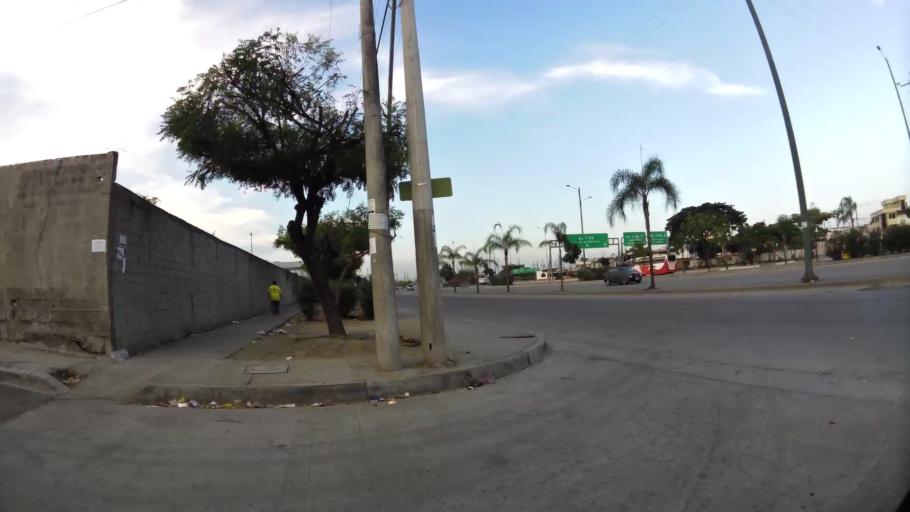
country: EC
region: Guayas
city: Eloy Alfaro
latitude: -2.1359
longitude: -79.8816
